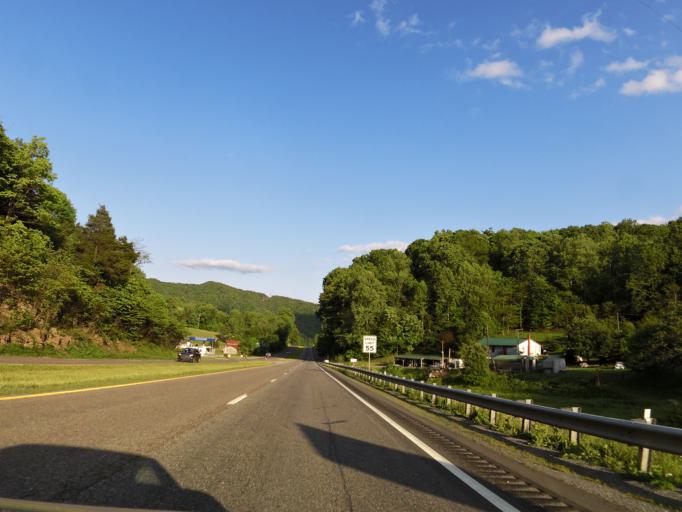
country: US
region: Virginia
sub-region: Russell County
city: Lebanon
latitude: 36.8149
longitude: -82.1109
